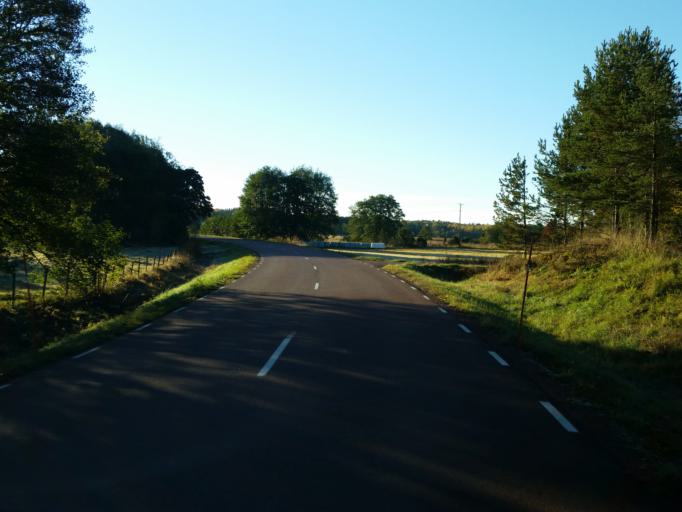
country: AX
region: Alands skaergard
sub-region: Vardoe
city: Vardoe
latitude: 60.2327
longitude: 20.3764
